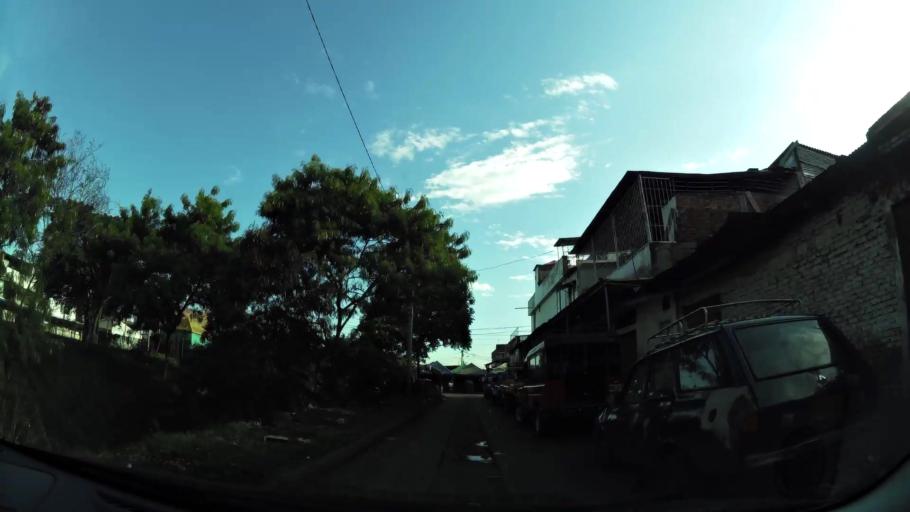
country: CO
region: Valle del Cauca
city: Cali
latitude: 3.4296
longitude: -76.5202
